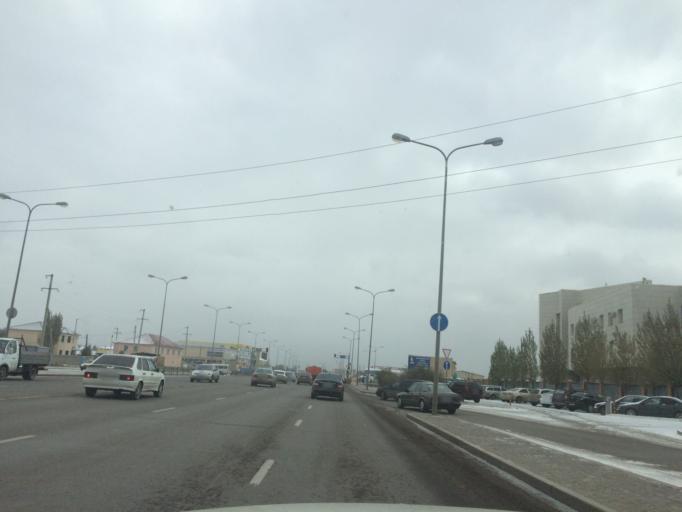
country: KZ
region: Astana Qalasy
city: Astana
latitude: 51.1774
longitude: 71.4723
